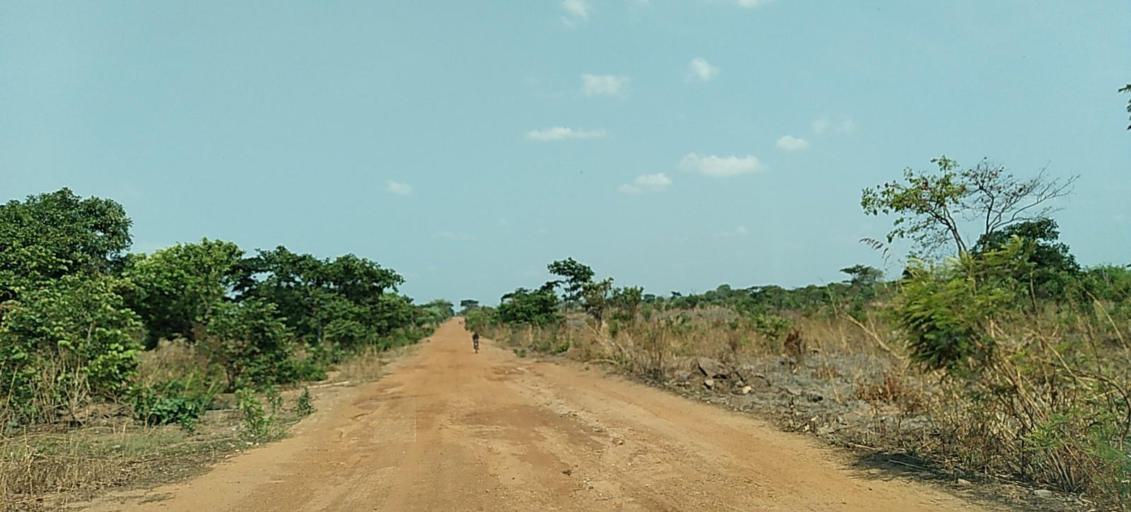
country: ZM
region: Copperbelt
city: Luanshya
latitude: -13.0918
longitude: 28.2965
